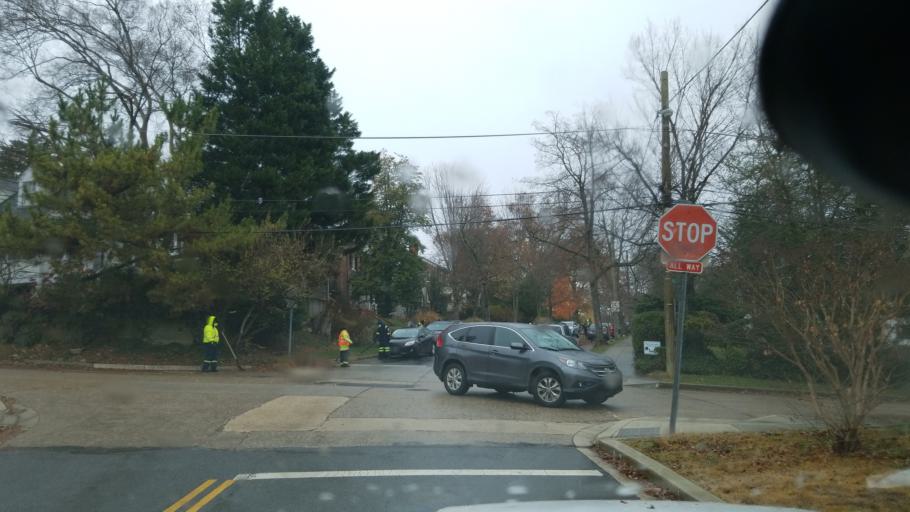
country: US
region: Maryland
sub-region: Montgomery County
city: Brookmont
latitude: 38.9273
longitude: -77.1079
